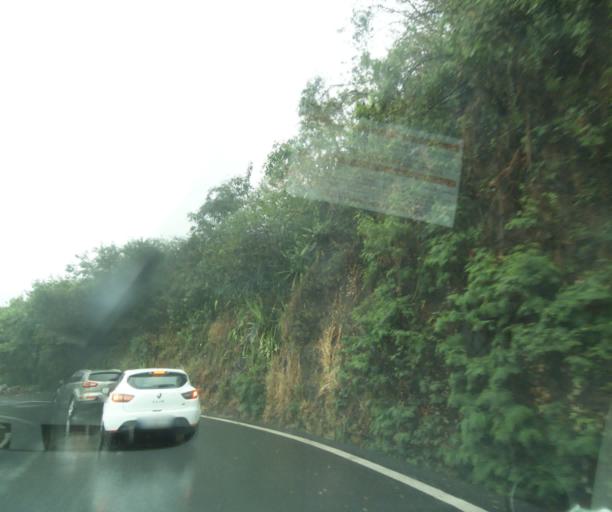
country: RE
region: Reunion
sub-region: Reunion
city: Saint-Paul
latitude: -21.0358
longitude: 55.2799
